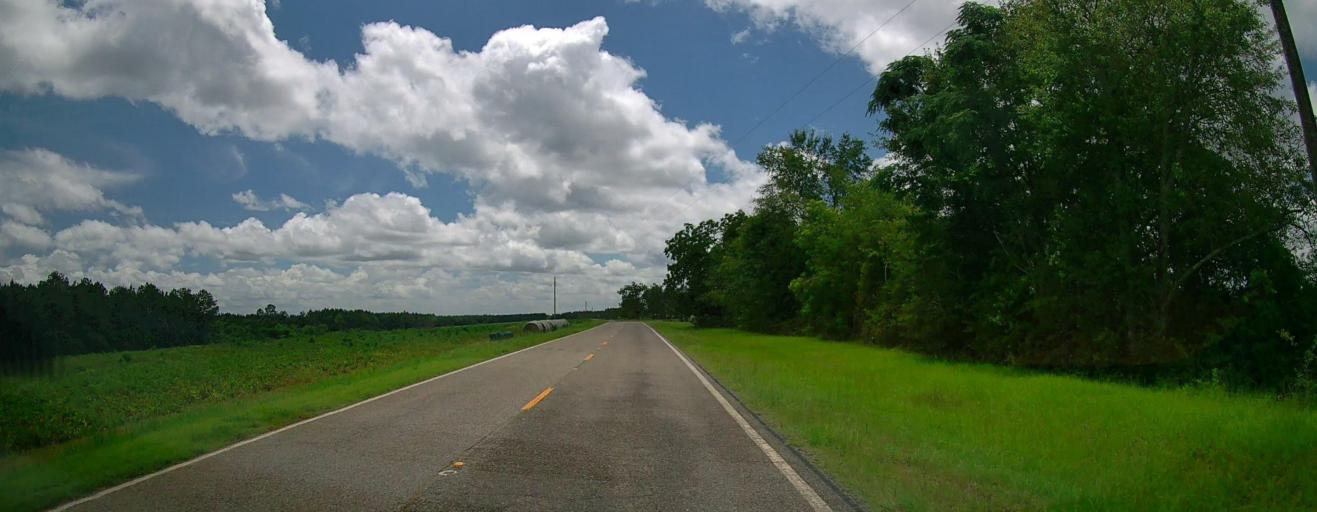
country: US
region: Georgia
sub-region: Wilcox County
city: Rochelle
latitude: 31.8853
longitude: -83.5560
